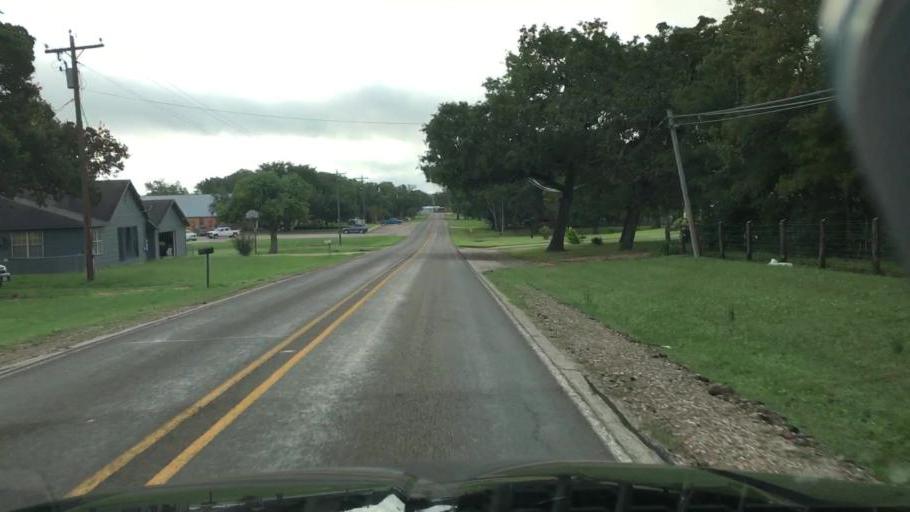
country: US
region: Texas
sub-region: Lee County
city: Lexington
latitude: 30.3620
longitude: -96.8312
